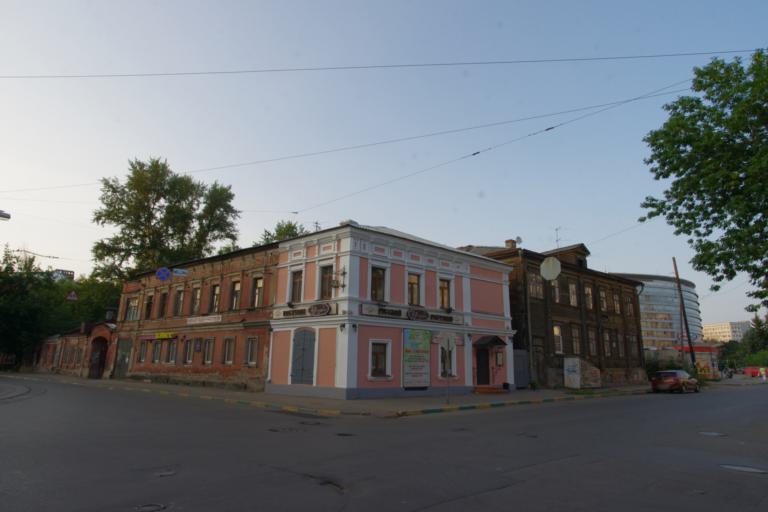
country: RU
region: Nizjnij Novgorod
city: Nizhniy Novgorod
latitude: 56.3223
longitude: 44.0079
